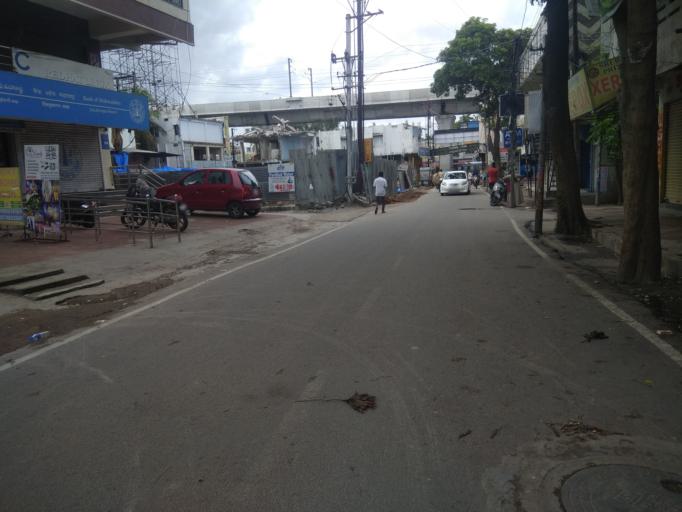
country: IN
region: Telangana
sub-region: Rangareddi
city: Gaddi Annaram
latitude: 17.3676
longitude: 78.5287
